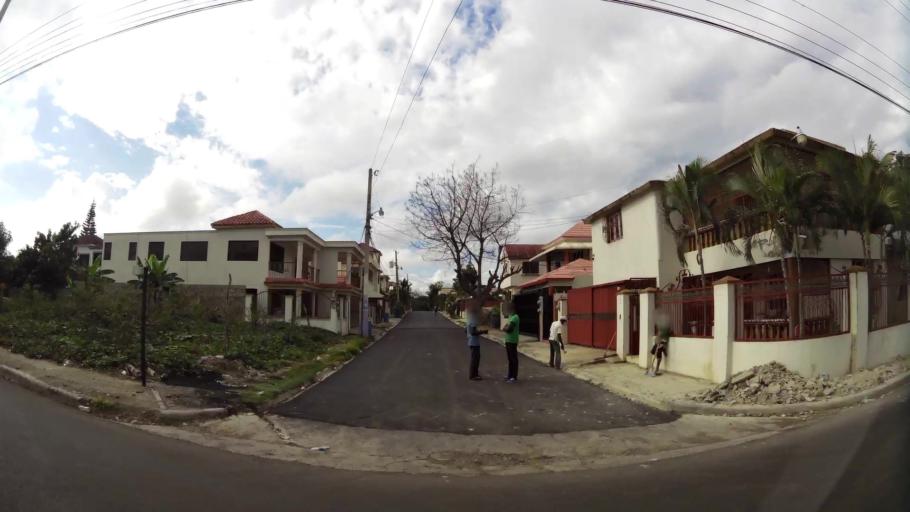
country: DO
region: Santiago
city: Santiago de los Caballeros
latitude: 19.4276
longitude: -70.6763
